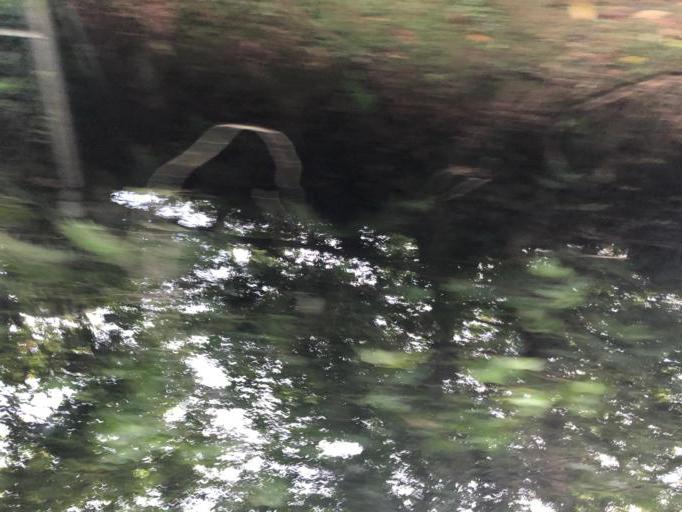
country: TW
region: Taiwan
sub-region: Keelung
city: Keelung
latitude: 25.1546
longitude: 121.6444
